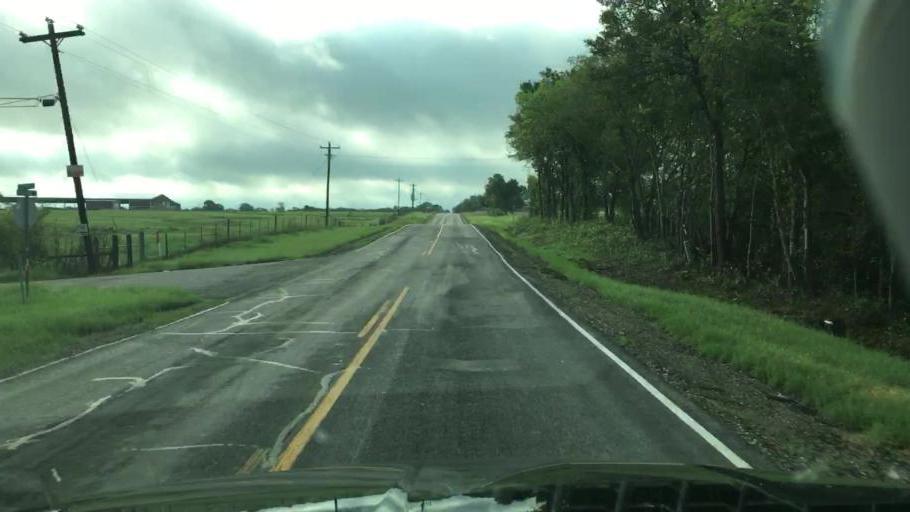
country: US
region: Texas
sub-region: Lee County
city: Lexington
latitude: 30.3693
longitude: -96.8401
